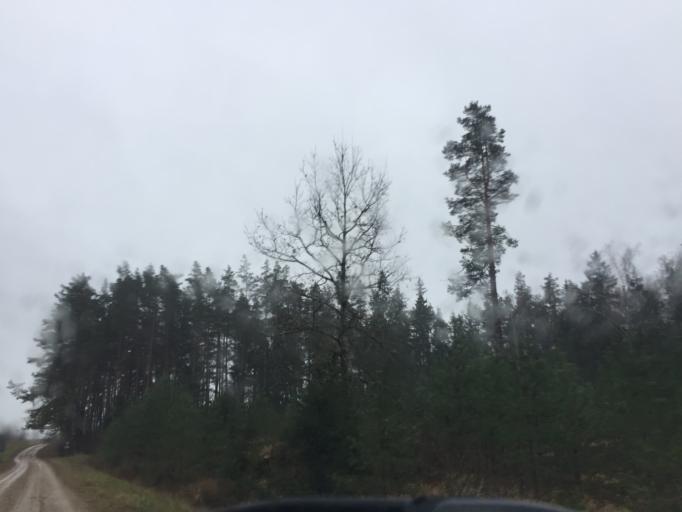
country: LV
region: Salas
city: Sala
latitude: 56.5063
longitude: 25.7015
